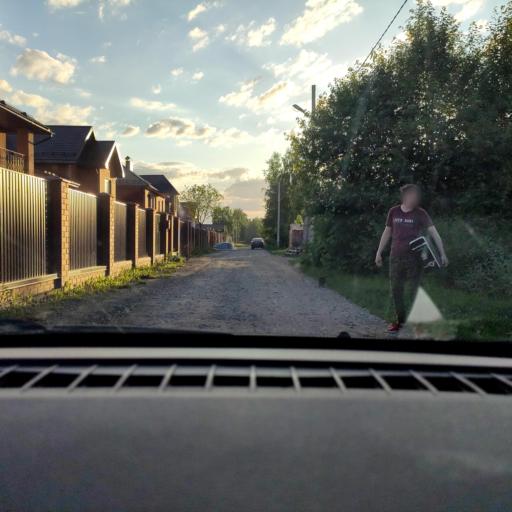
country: RU
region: Perm
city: Polazna
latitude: 58.1293
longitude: 56.3984
